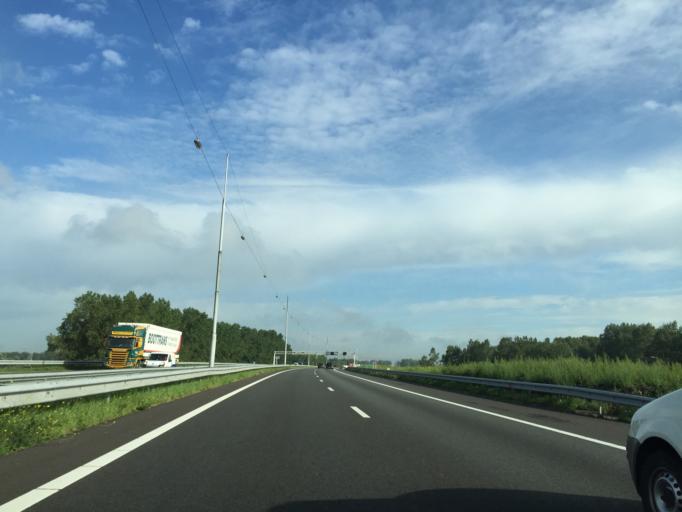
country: NL
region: North Holland
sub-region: Gemeente Velsen
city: Velsen-Zuid
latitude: 52.4400
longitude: 4.6693
